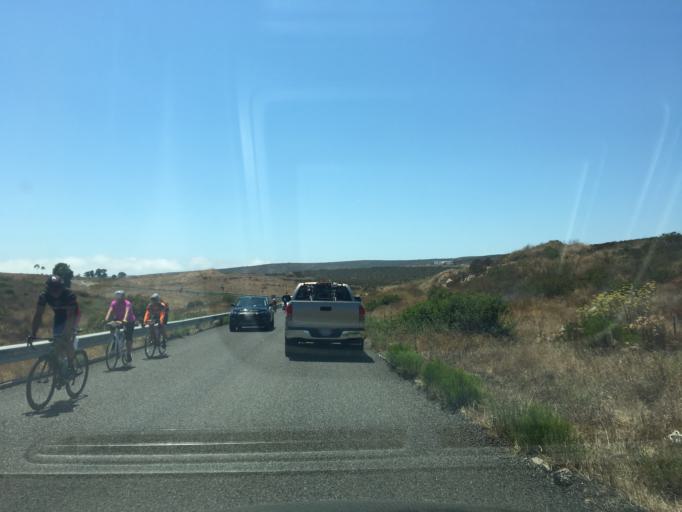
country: MX
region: Baja California
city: El Sauzal
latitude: 31.9934
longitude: -116.6954
